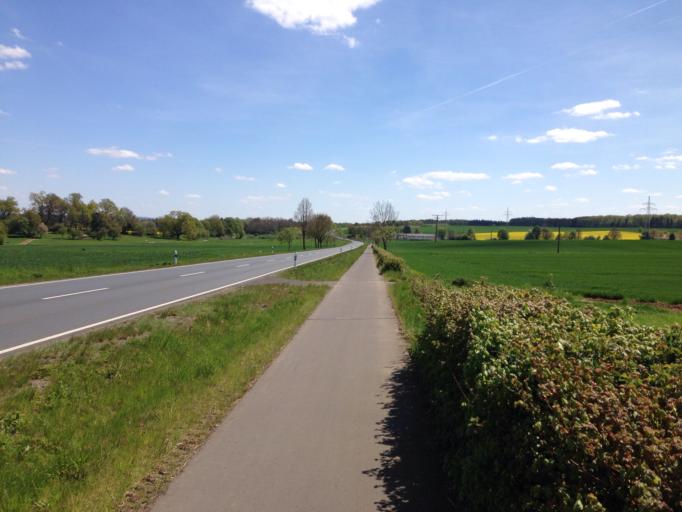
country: DE
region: Hesse
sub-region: Regierungsbezirk Giessen
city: Hungen
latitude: 50.4822
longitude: 8.8687
